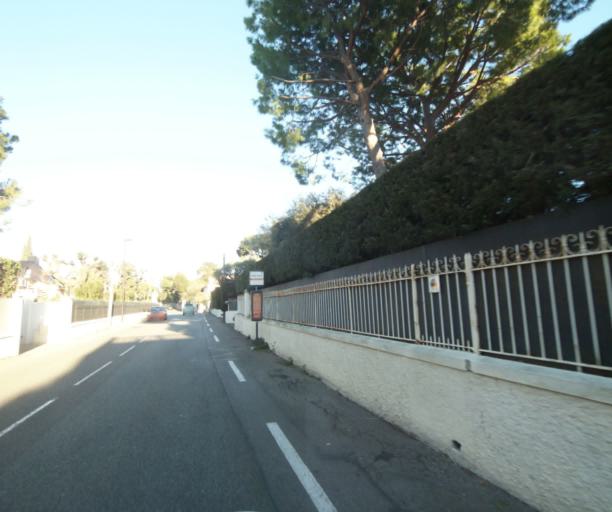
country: FR
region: Provence-Alpes-Cote d'Azur
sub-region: Departement des Alpes-Maritimes
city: Antibes
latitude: 43.5505
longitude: 7.1259
